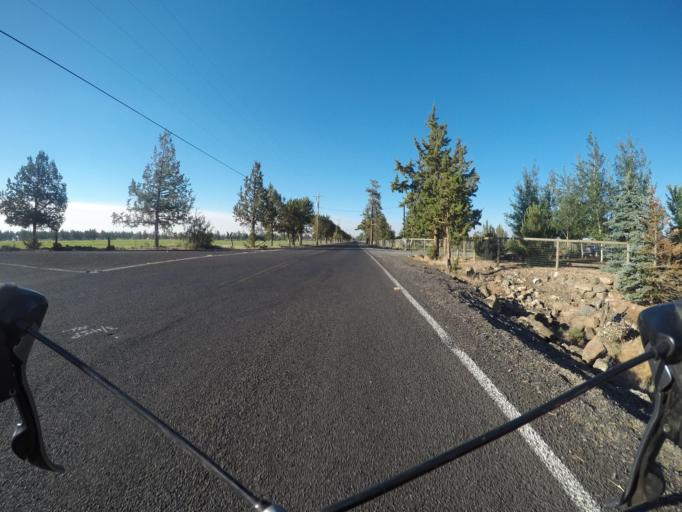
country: US
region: Oregon
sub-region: Deschutes County
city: Redmond
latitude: 44.2475
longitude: -121.2396
